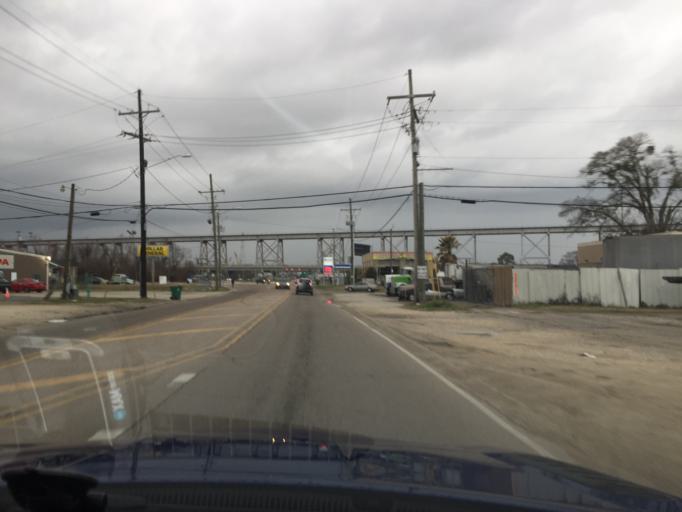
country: US
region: Louisiana
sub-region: Jefferson Parish
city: Bridge City
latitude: 29.9301
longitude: -90.1616
